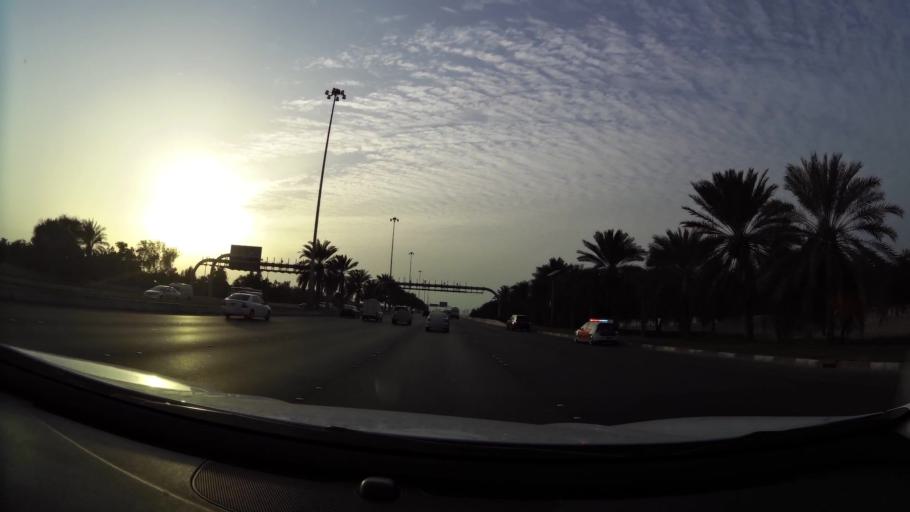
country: AE
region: Abu Dhabi
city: Abu Dhabi
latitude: 24.4011
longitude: 54.4952
